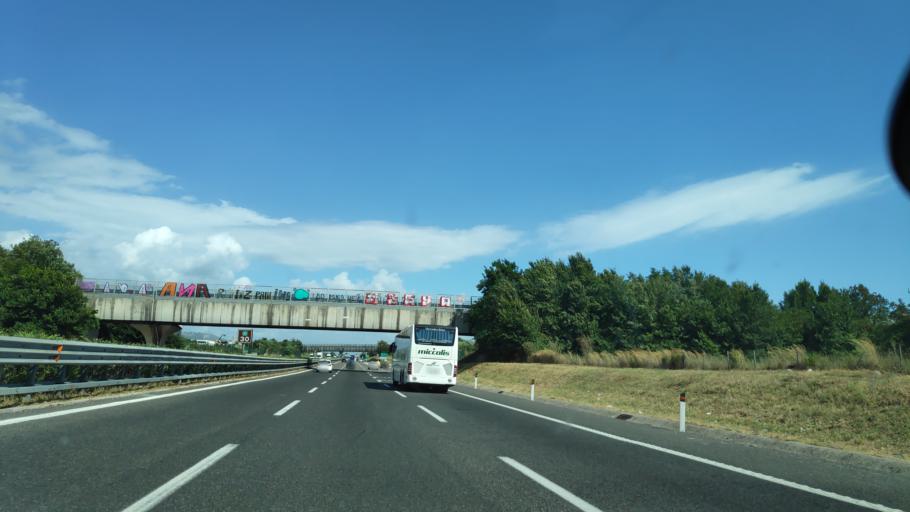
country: IT
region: Campania
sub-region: Provincia di Salerno
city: Pagliarone
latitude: 40.6351
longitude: 14.9138
